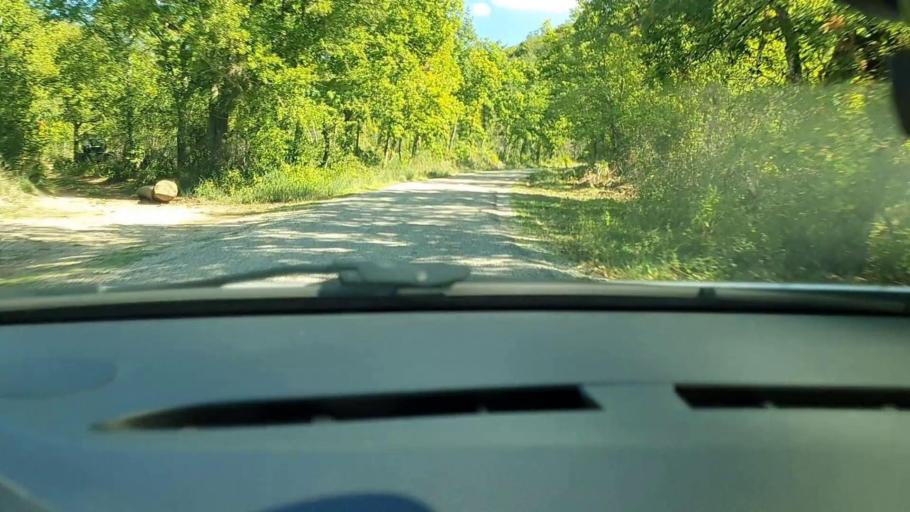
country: FR
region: Languedoc-Roussillon
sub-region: Departement du Gard
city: Saint-Ambroix
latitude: 44.2074
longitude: 4.2988
